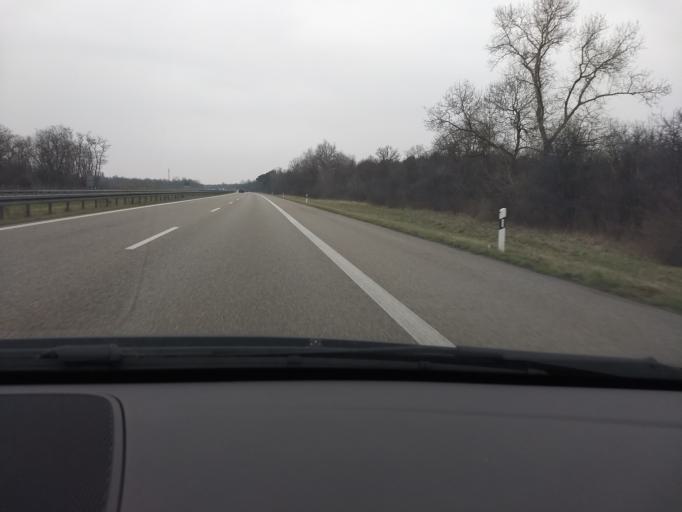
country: DE
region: Baden-Wuerttemberg
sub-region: Freiburg Region
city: Neuenburg am Rhein
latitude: 47.8342
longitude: 7.5649
